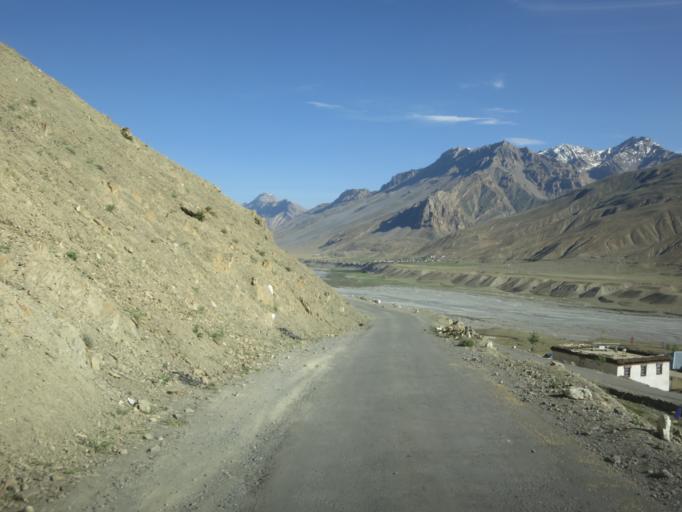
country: IN
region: Himachal Pradesh
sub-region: Shimla
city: Sarahan
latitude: 32.2906
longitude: 78.0139
